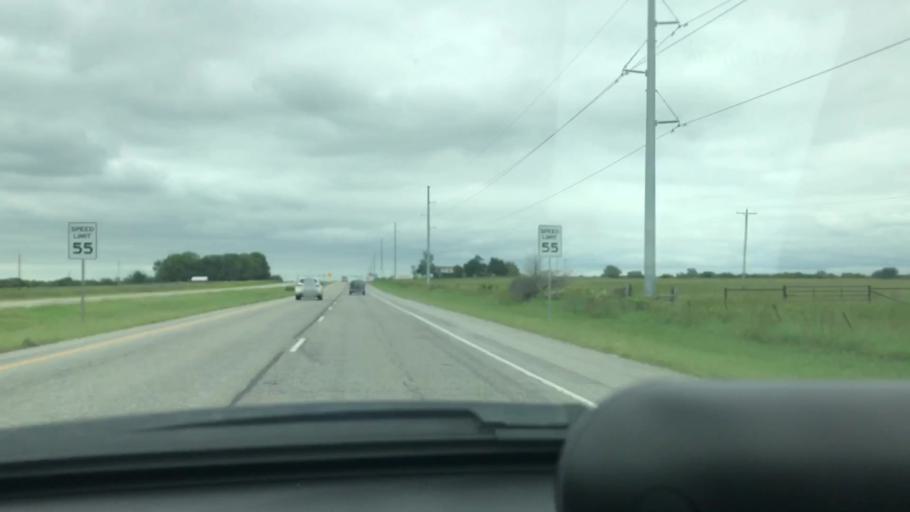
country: US
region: Oklahoma
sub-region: Wagoner County
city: Wagoner
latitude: 36.0114
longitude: -95.3686
